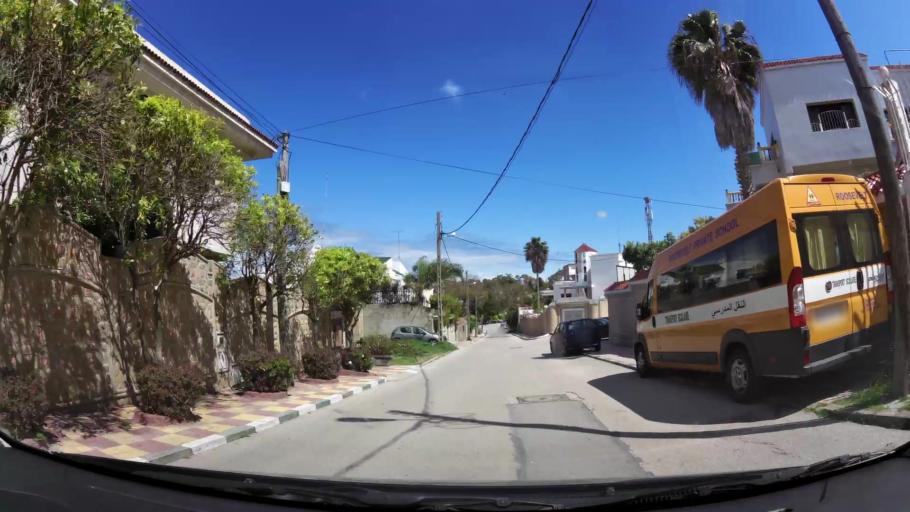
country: MA
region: Tanger-Tetouan
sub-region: Tanger-Assilah
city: Tangier
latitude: 35.7785
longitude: -5.8374
